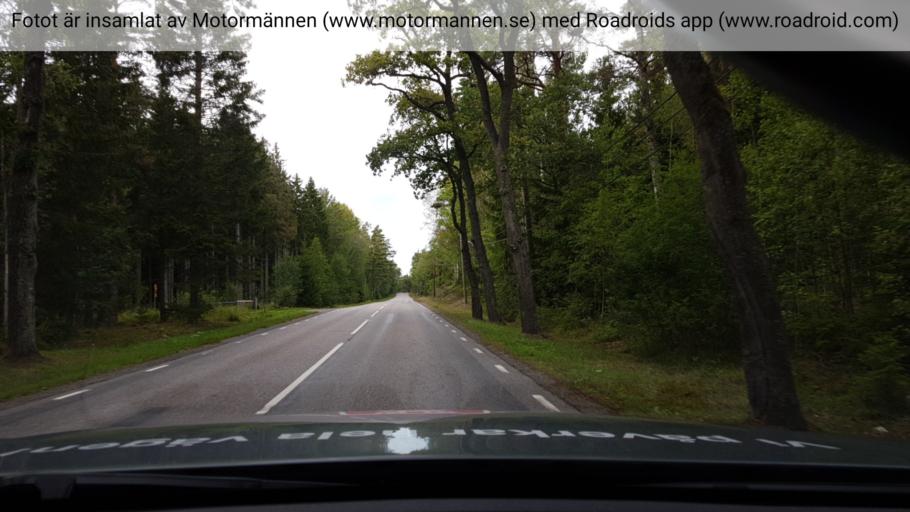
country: SE
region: Stockholm
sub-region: Haninge Kommun
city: Haninge
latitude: 59.1167
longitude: 18.1894
